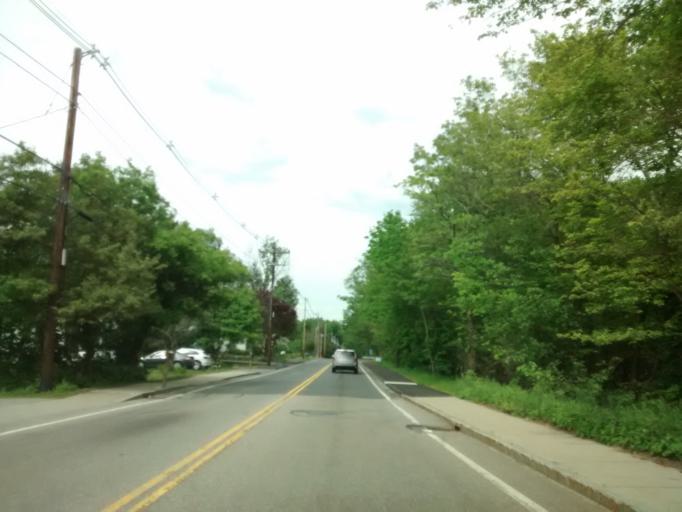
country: US
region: Massachusetts
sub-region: Middlesex County
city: Hopkinton
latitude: 42.2186
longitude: -71.5394
